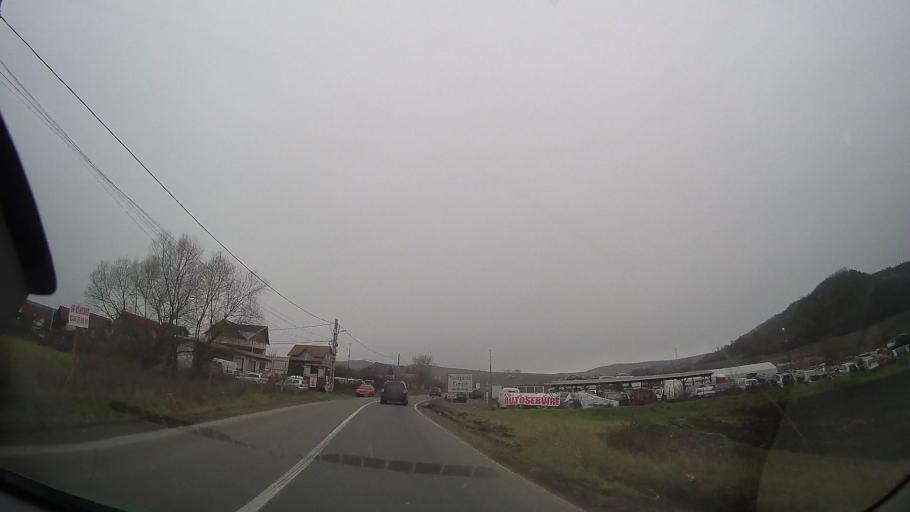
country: RO
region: Mures
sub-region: Comuna Ceausu de Campie
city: Ceausu de Campie
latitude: 46.6316
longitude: 24.5190
